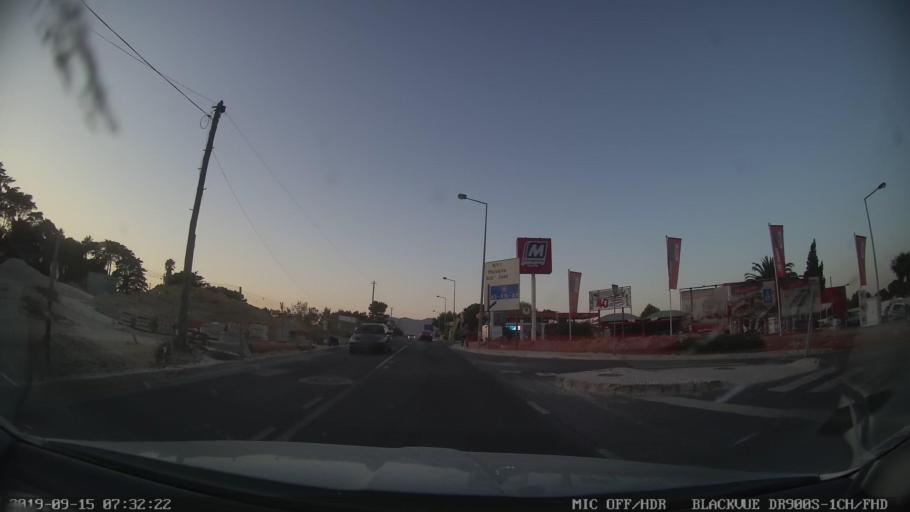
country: PT
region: Lisbon
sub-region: Cascais
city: Cascais
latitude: 38.7189
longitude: -9.4413
